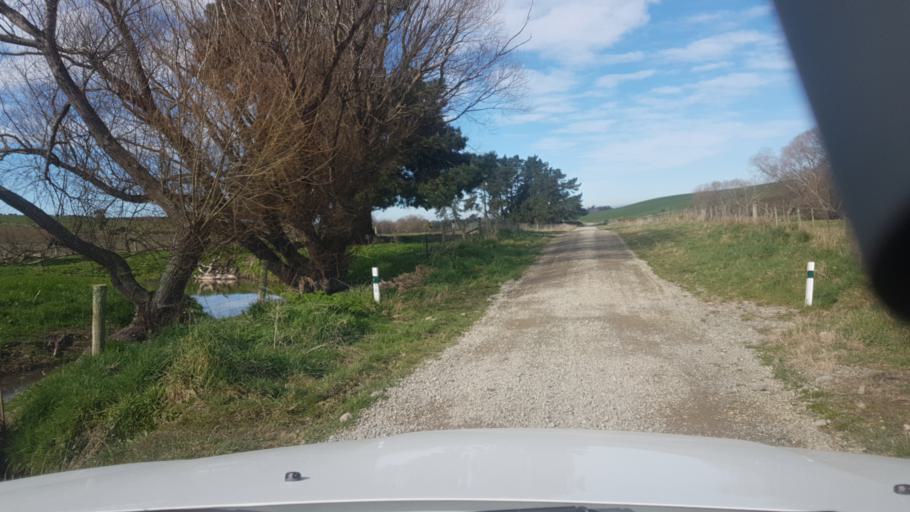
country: NZ
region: Canterbury
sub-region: Timaru District
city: Pleasant Point
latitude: -44.2002
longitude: 171.1829
